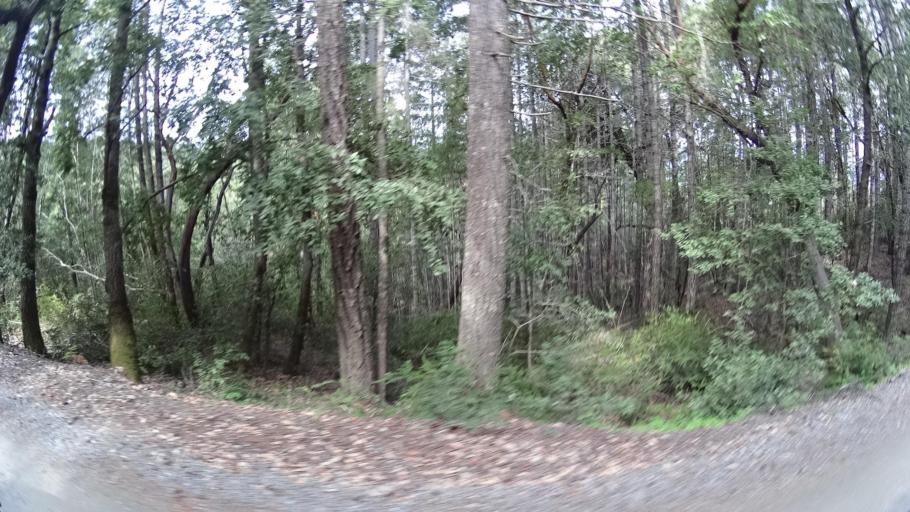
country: US
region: California
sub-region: Humboldt County
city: Redway
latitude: 40.0455
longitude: -123.8406
